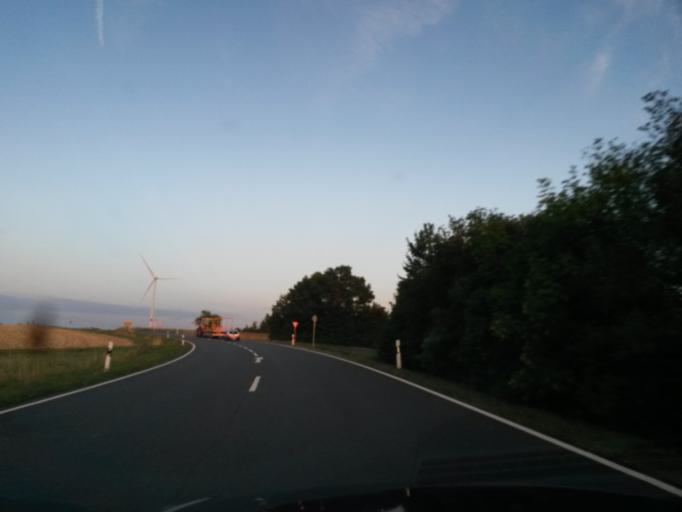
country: DE
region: Bavaria
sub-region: Regierungsbezirk Unterfranken
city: Holzkirchen
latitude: 49.8056
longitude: 9.6486
